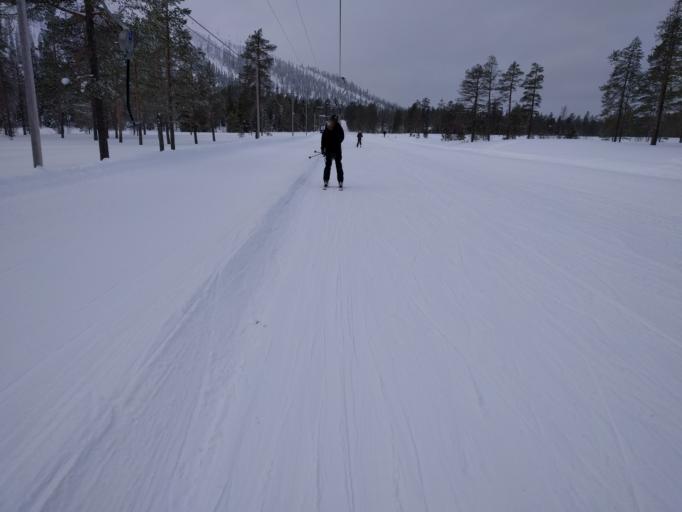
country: NO
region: Hedmark
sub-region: Trysil
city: Innbygda
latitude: 61.1737
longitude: 12.9901
